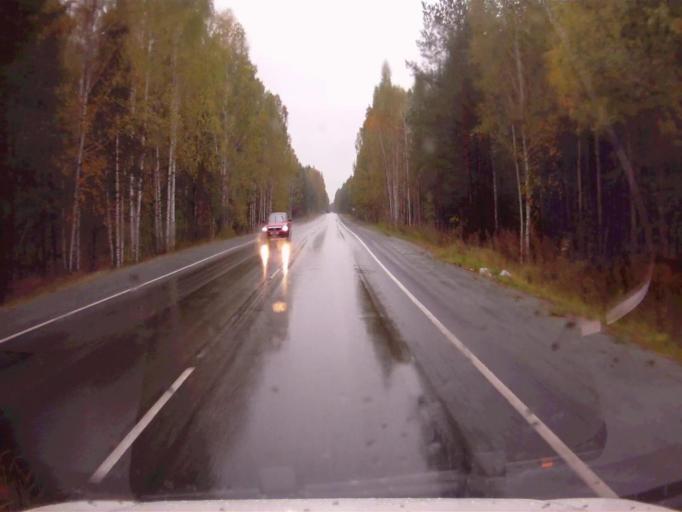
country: RU
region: Chelyabinsk
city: Tayginka
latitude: 55.5811
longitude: 60.6404
